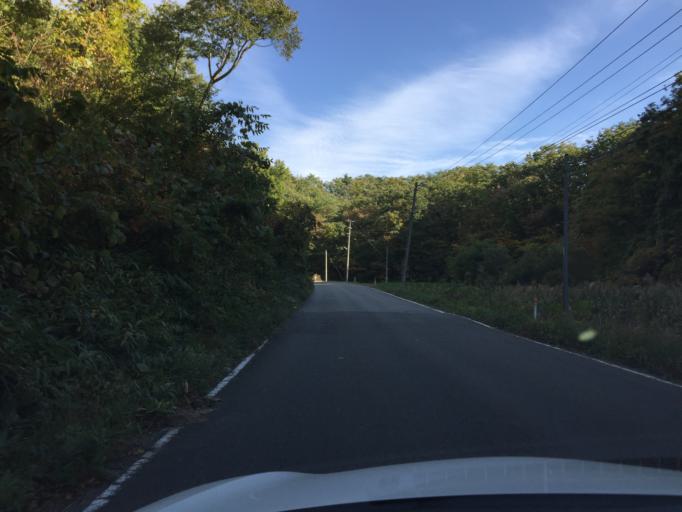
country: JP
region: Fukushima
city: Miharu
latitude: 37.3588
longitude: 140.5329
